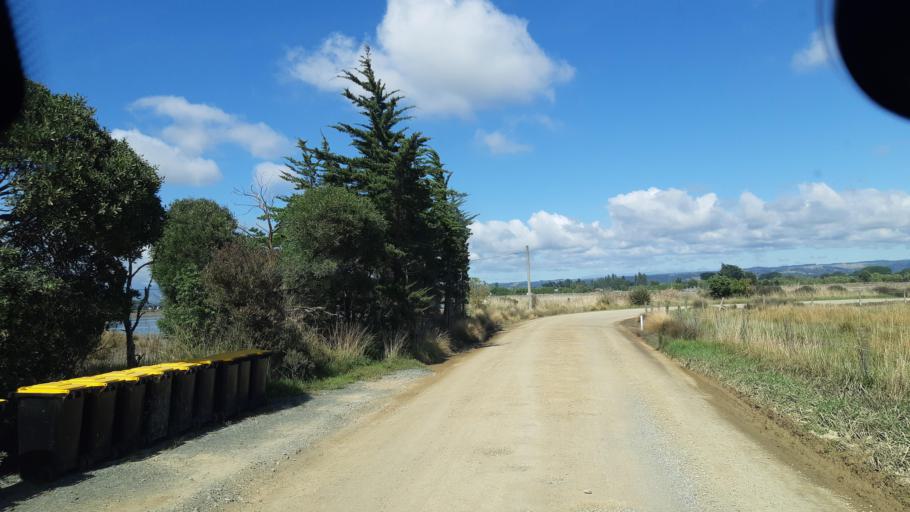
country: NZ
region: Tasman
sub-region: Tasman District
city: Richmond
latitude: -41.2996
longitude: 173.1599
